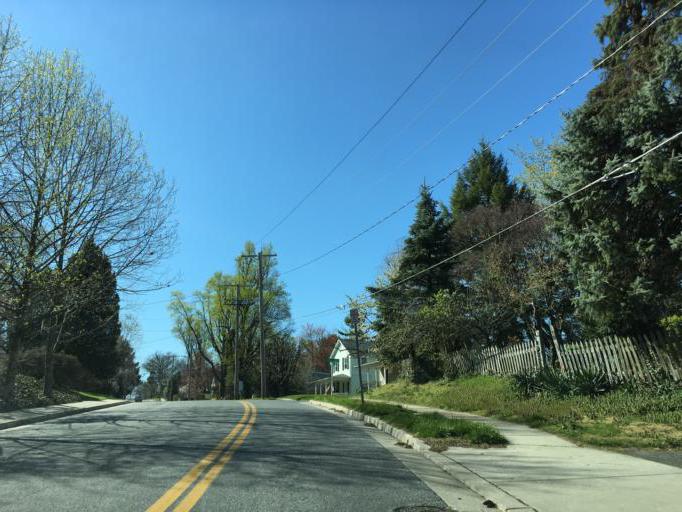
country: US
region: Maryland
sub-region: Baltimore County
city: Towson
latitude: 39.3752
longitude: -76.5877
